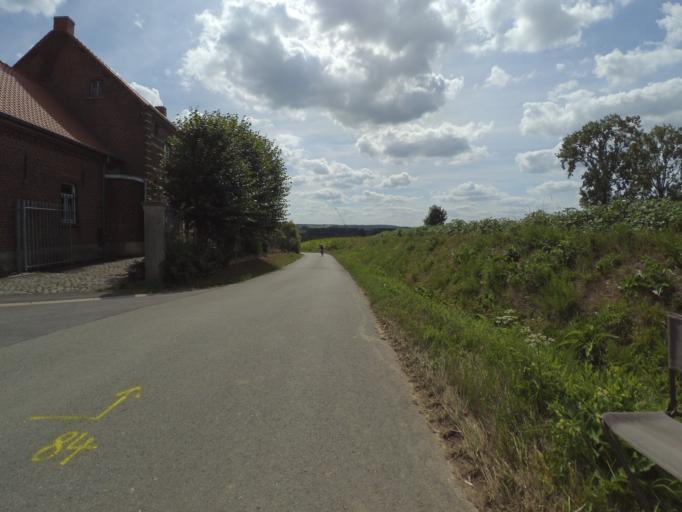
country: BE
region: Wallonia
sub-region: Province du Hainaut
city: Ellezelles
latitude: 50.8163
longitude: 3.6869
